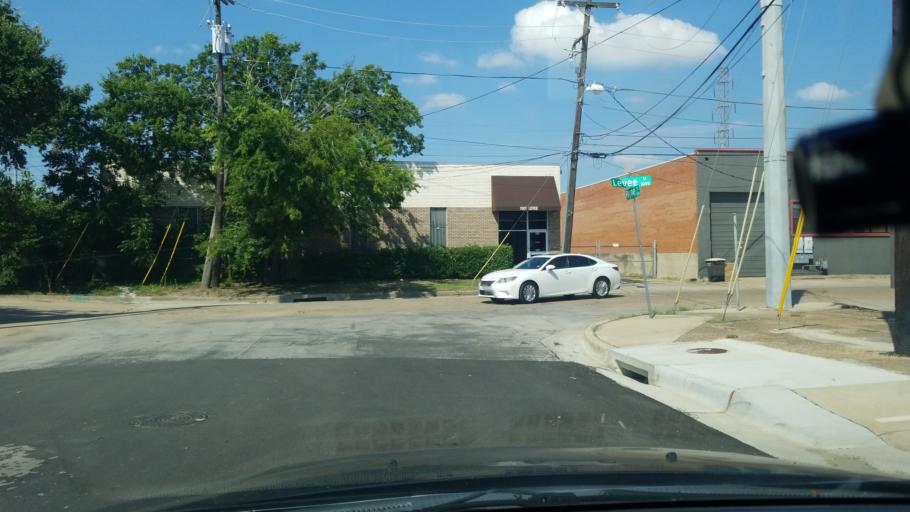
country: US
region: Texas
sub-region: Dallas County
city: Dallas
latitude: 32.7848
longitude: -96.8203
